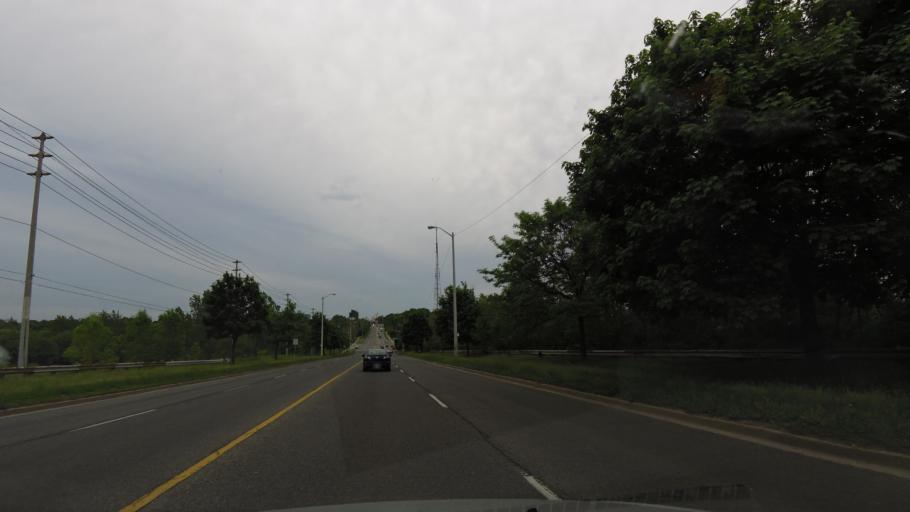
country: CA
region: Ontario
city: Etobicoke
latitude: 43.6873
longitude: -79.4998
